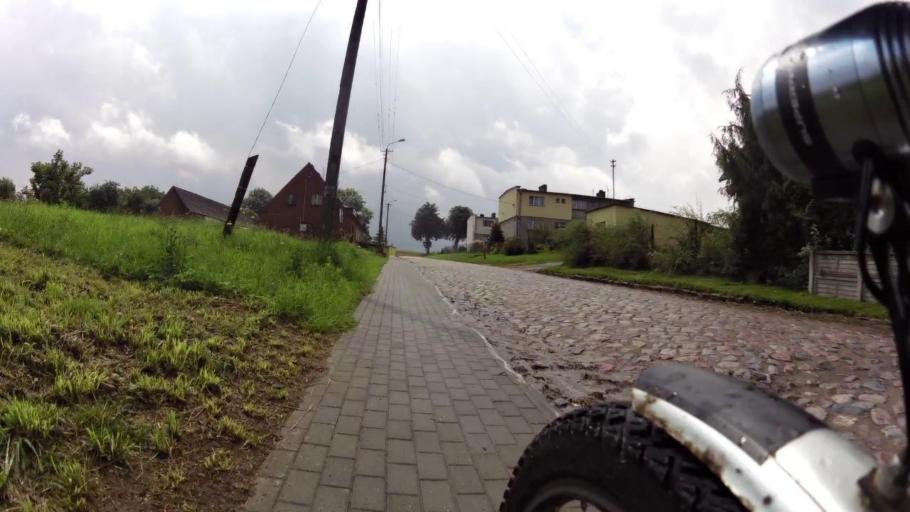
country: PL
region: West Pomeranian Voivodeship
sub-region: Powiat lobeski
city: Lobez
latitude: 53.7331
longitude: 15.6752
